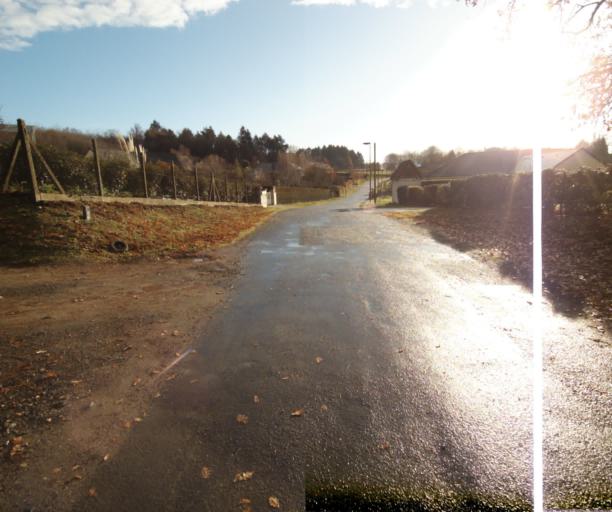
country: FR
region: Limousin
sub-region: Departement de la Correze
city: Saint-Mexant
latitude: 45.2703
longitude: 1.6391
